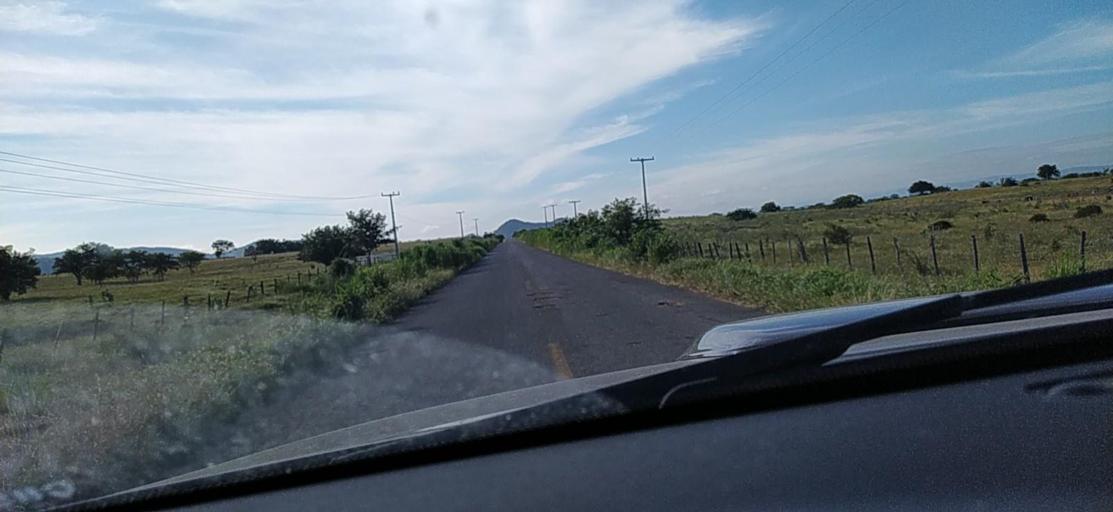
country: BR
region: Bahia
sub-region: Guanambi
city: Guanambi
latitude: -14.0760
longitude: -42.8790
